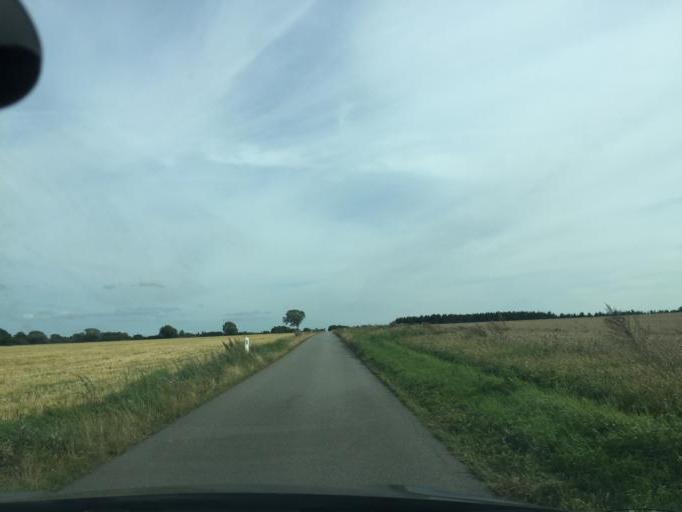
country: DK
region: South Denmark
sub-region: Kerteminde Kommune
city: Langeskov
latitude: 55.3389
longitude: 10.5497
